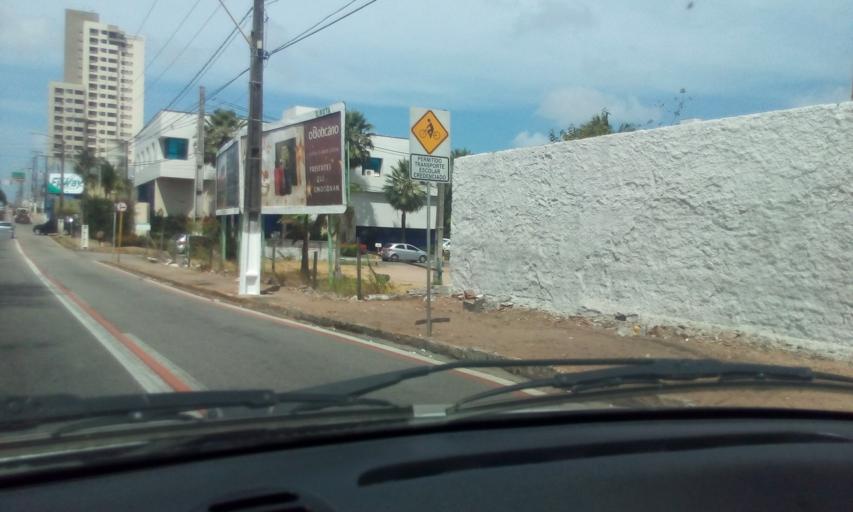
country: BR
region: Rio Grande do Norte
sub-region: Natal
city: Natal
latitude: -5.8206
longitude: -35.2132
